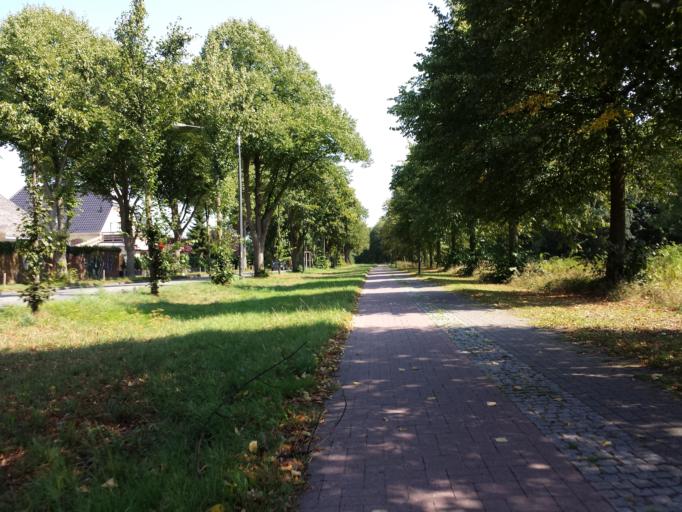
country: DE
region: Bremen
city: Bremen
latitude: 53.0505
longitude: 8.8404
